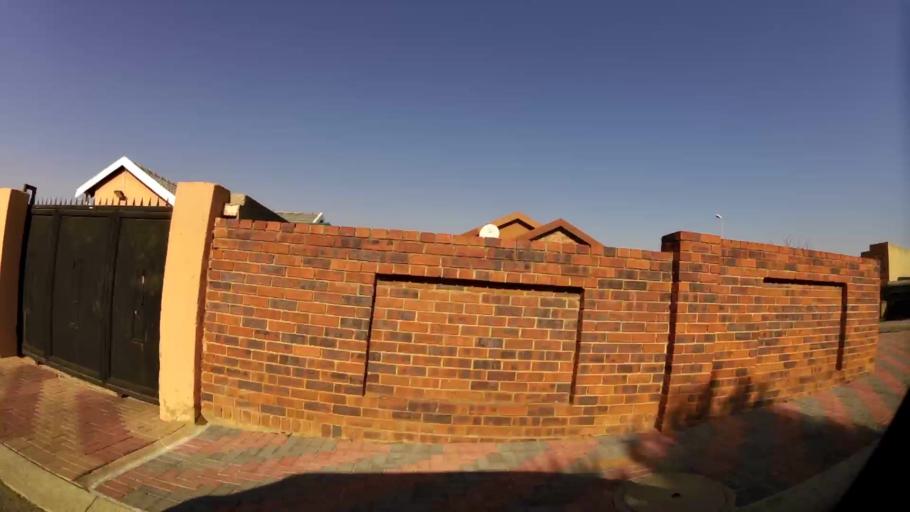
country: ZA
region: Gauteng
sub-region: City of Johannesburg Metropolitan Municipality
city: Soweto
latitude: -26.2933
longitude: 27.9498
